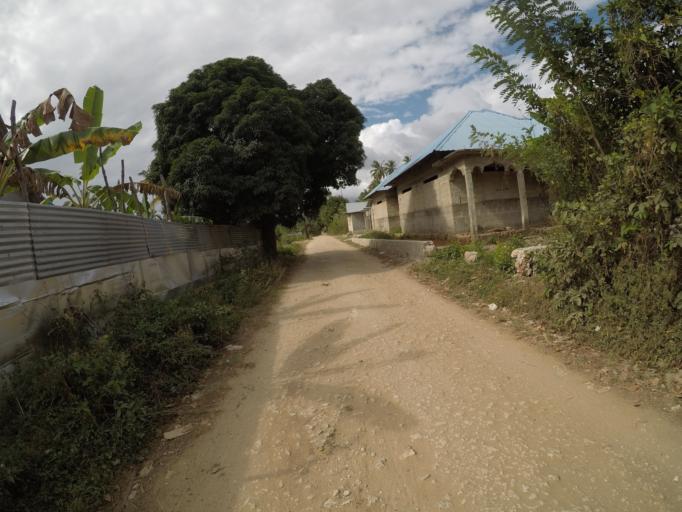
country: TZ
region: Zanzibar Central/South
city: Koani
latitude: -6.1906
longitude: 39.2639
